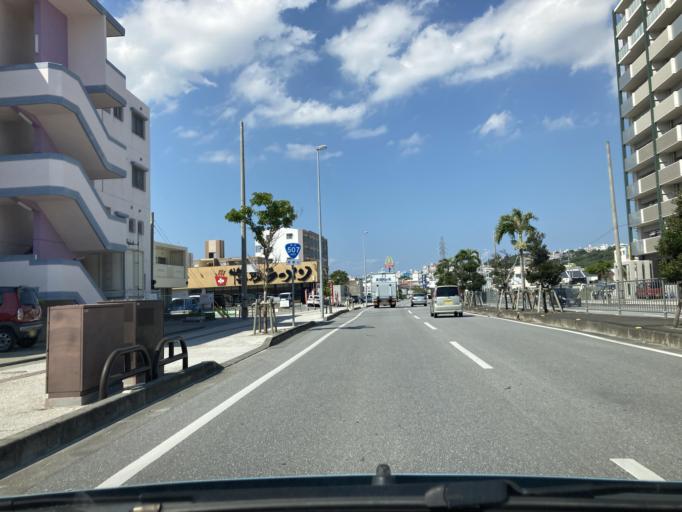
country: JP
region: Okinawa
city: Tomigusuku
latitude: 26.1909
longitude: 127.7153
